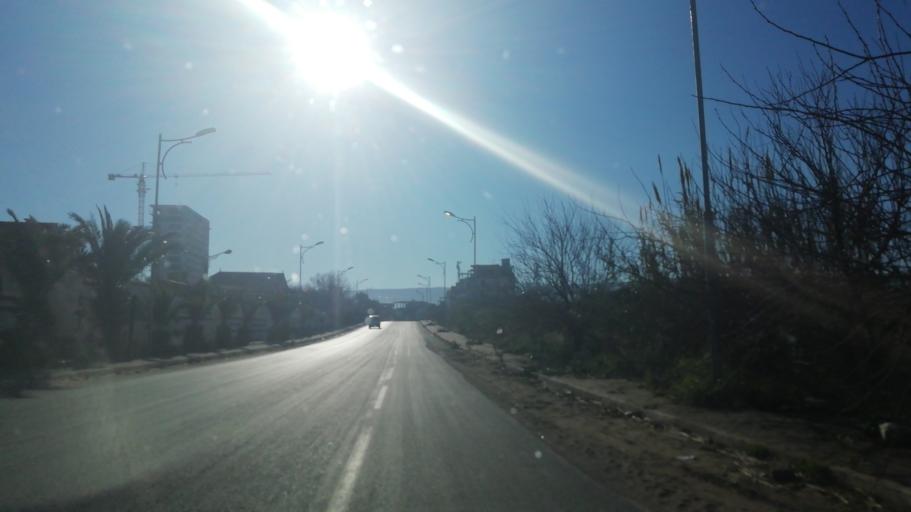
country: DZ
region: Oran
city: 'Ain el Turk
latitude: 35.7574
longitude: -0.7907
